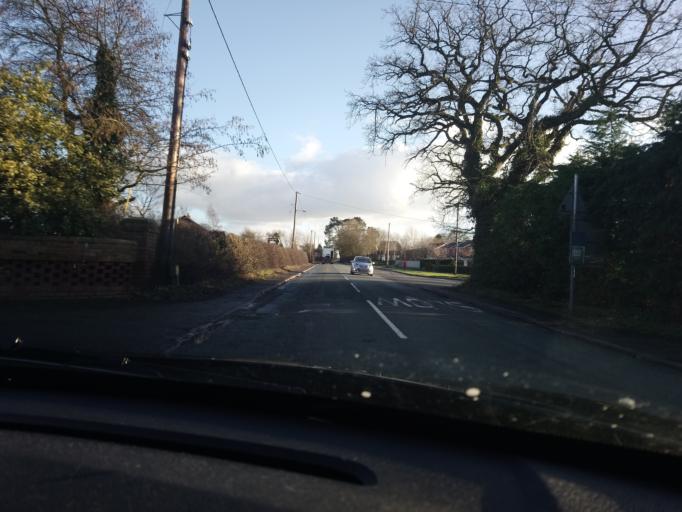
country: GB
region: England
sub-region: Shropshire
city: Ellesmere
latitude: 52.9162
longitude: -2.9158
